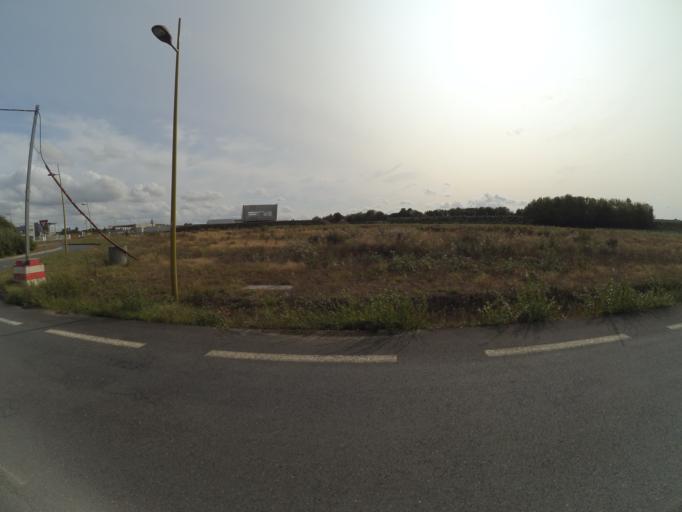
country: FR
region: Pays de la Loire
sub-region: Departement de la Vendee
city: Bouffere
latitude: 46.9512
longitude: -1.3446
